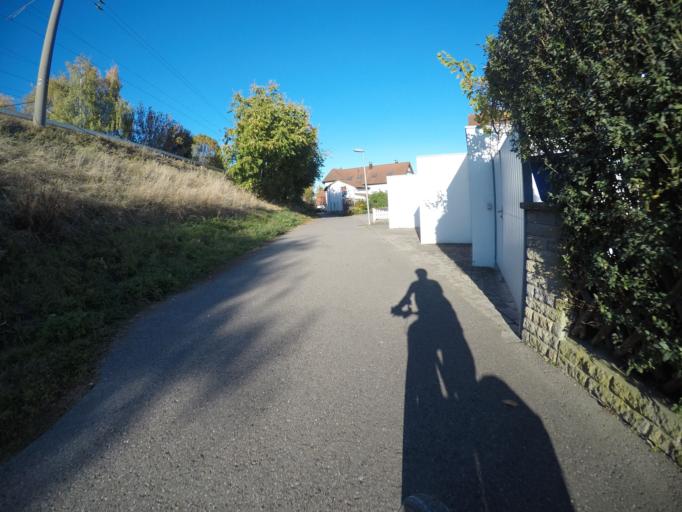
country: DE
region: Baden-Wuerttemberg
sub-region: Regierungsbezirk Stuttgart
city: Nufringen
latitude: 48.6220
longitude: 8.8931
